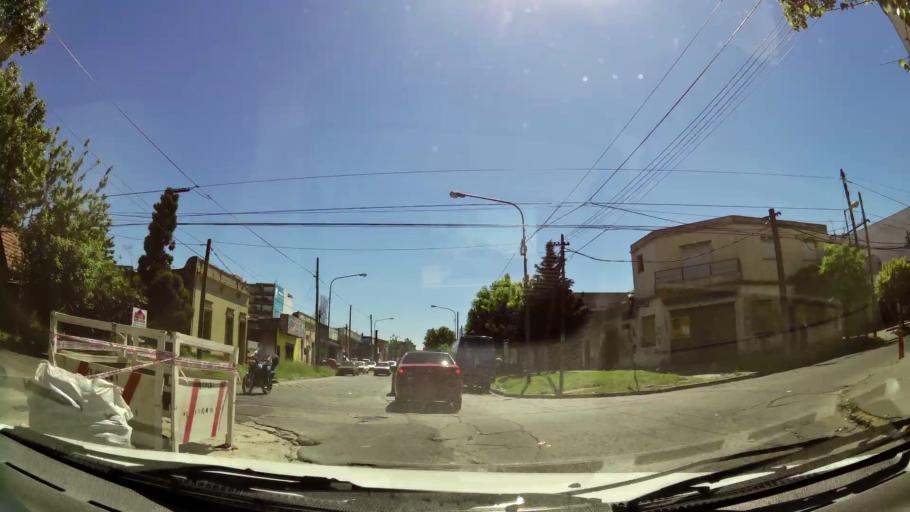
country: AR
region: Buenos Aires
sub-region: Partido de General San Martin
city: General San Martin
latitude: -34.5788
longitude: -58.5303
